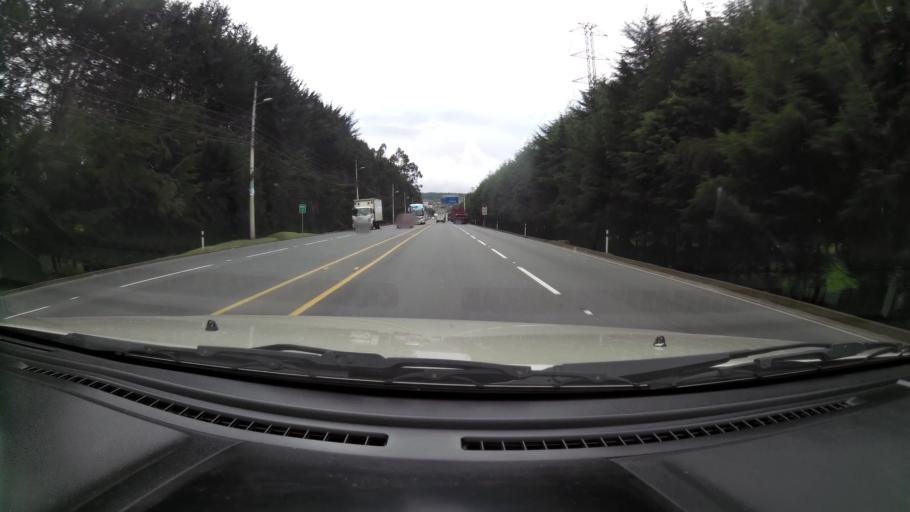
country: EC
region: Pichincha
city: Machachi
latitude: -0.4674
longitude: -78.5860
